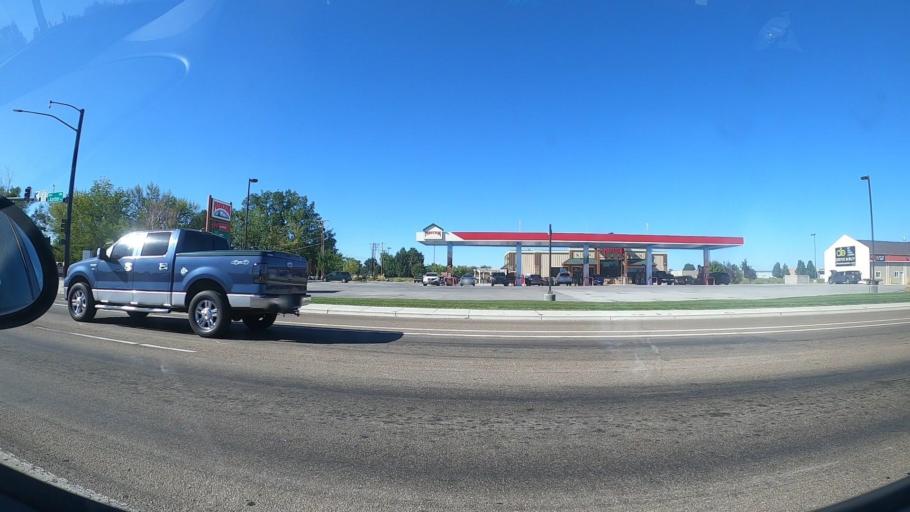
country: US
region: Idaho
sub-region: Canyon County
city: Nampa
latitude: 43.6050
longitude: -116.6106
